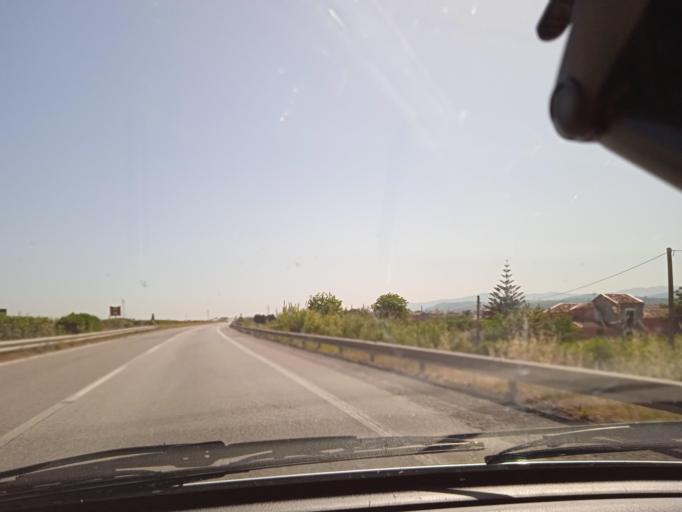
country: IT
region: Sicily
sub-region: Messina
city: Barcellona Pozzo di Gotto
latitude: 38.1667
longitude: 15.2157
